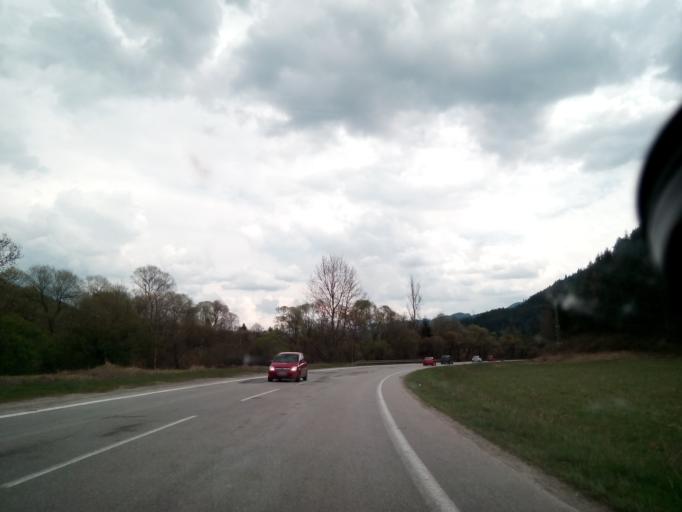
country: SK
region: Zilinsky
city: Ruzomberok
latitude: 49.1061
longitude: 19.2391
